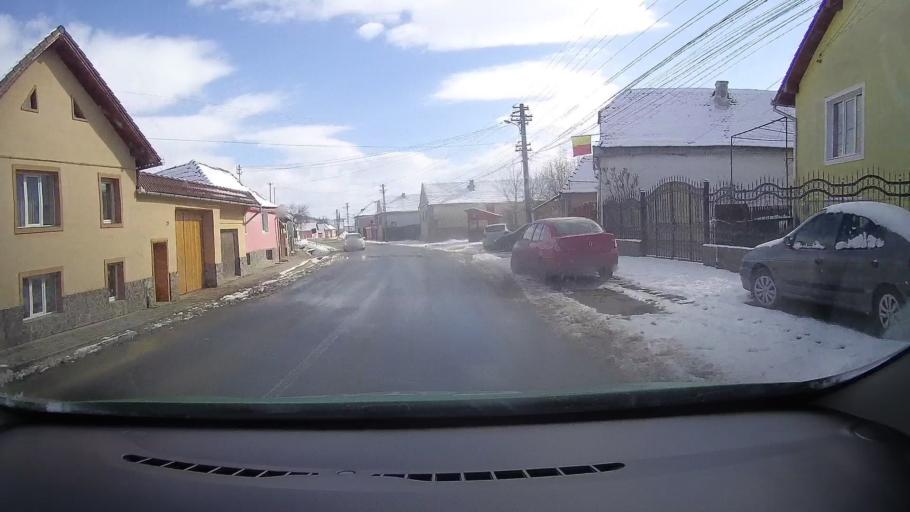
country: RO
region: Sibiu
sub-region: Comuna Barghis
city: Barghis
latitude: 45.9817
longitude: 24.5376
